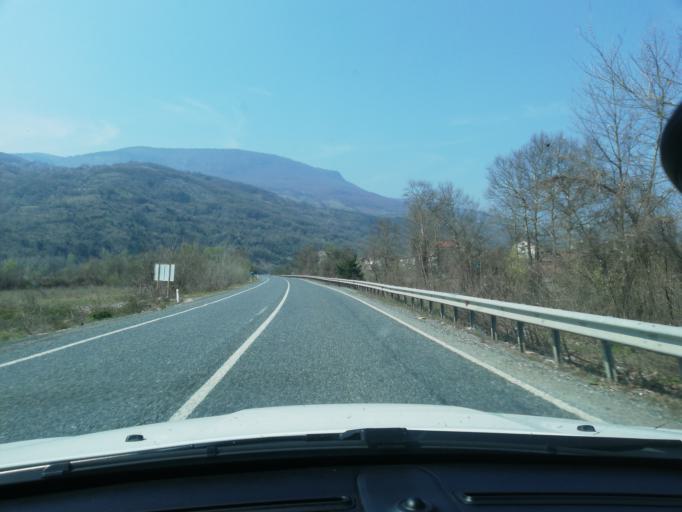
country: TR
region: Karabuk
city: Yenice
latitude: 41.2135
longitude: 32.2766
